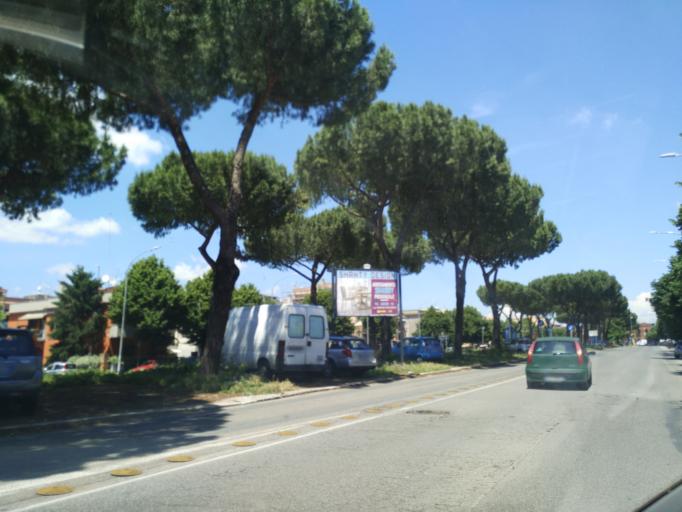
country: IT
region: Latium
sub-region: Citta metropolitana di Roma Capitale
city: Rome
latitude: 41.8747
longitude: 12.5706
